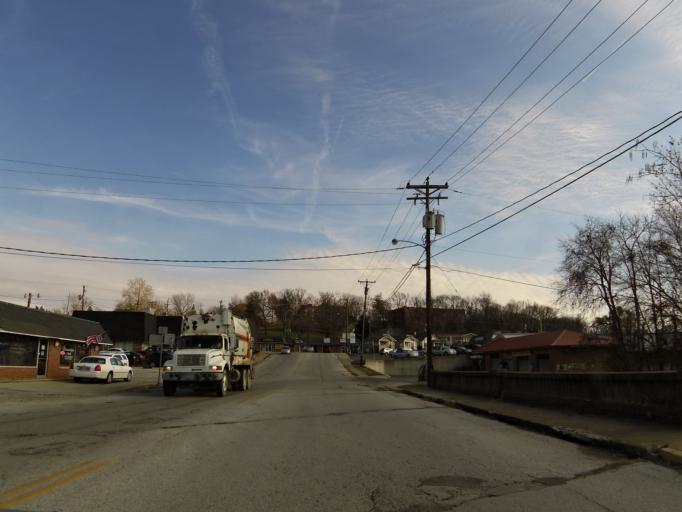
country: US
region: Missouri
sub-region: Marion County
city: Hannibal
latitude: 39.7059
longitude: -91.3877
